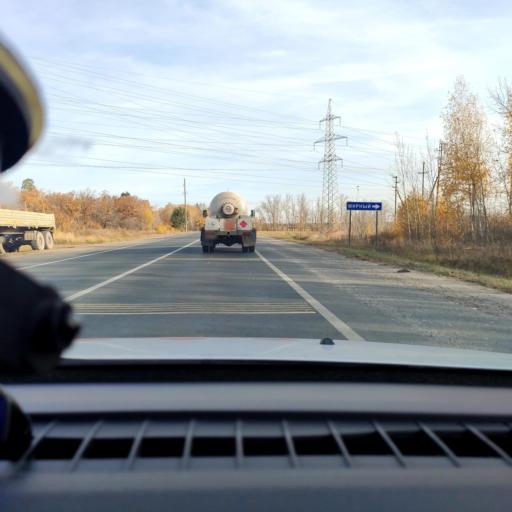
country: RU
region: Samara
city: Volzhskiy
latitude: 53.4493
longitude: 50.1242
